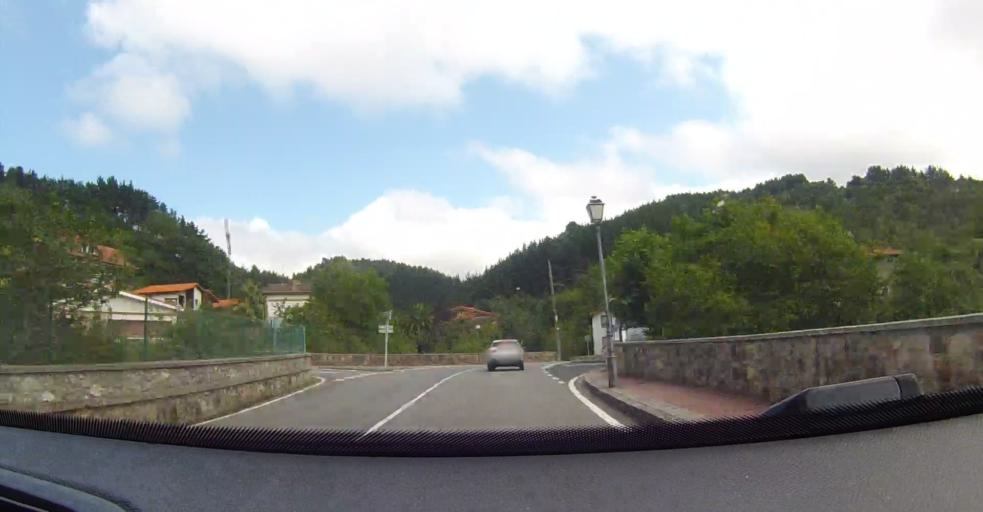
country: ES
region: Basque Country
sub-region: Bizkaia
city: Ibarrangelu
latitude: 43.3888
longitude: -2.6319
